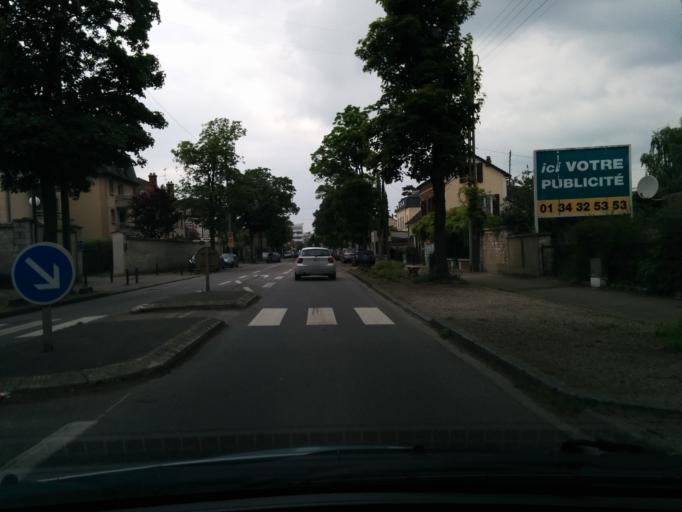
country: FR
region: Haute-Normandie
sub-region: Departement de l'Eure
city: Vernon
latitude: 49.0886
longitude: 1.4931
